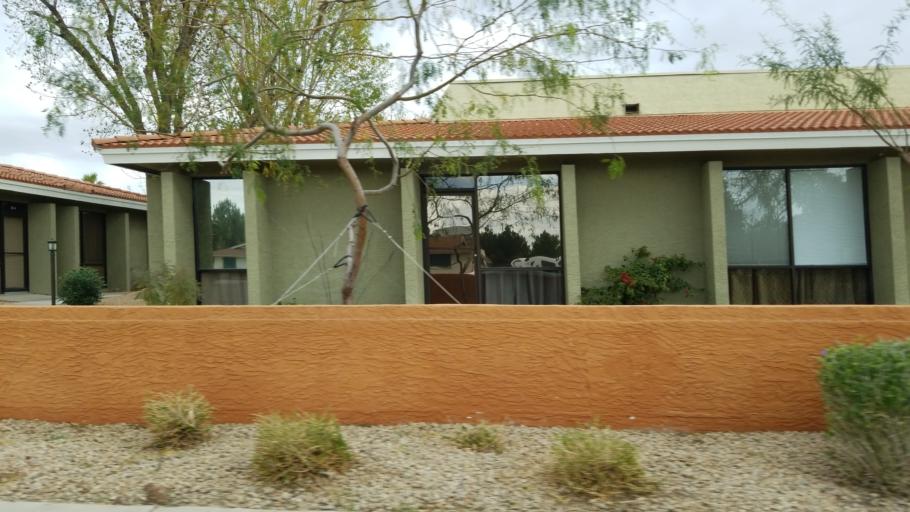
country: US
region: Arizona
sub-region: Maricopa County
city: Glendale
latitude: 33.5622
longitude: -112.1862
